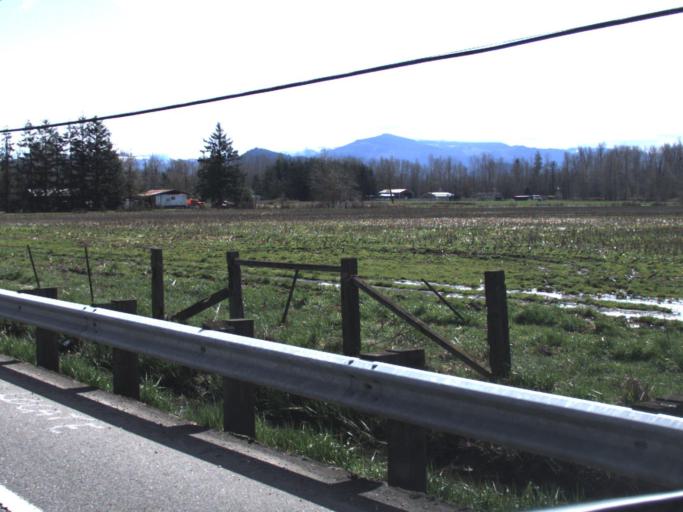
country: US
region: Washington
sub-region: Pierce County
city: Buckley
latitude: 47.2101
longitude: -122.0562
